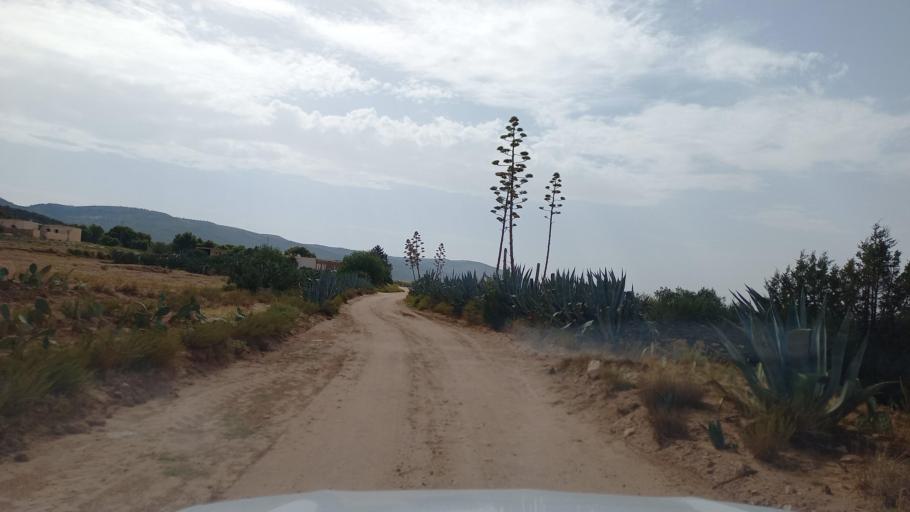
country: TN
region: Al Qasrayn
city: Kasserine
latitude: 35.3491
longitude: 8.8709
